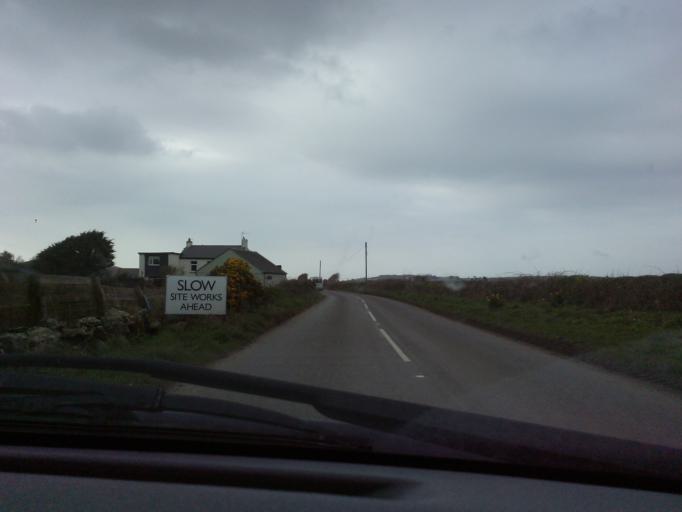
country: GB
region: England
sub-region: Cornwall
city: Saint Just
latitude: 50.1007
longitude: -5.6660
